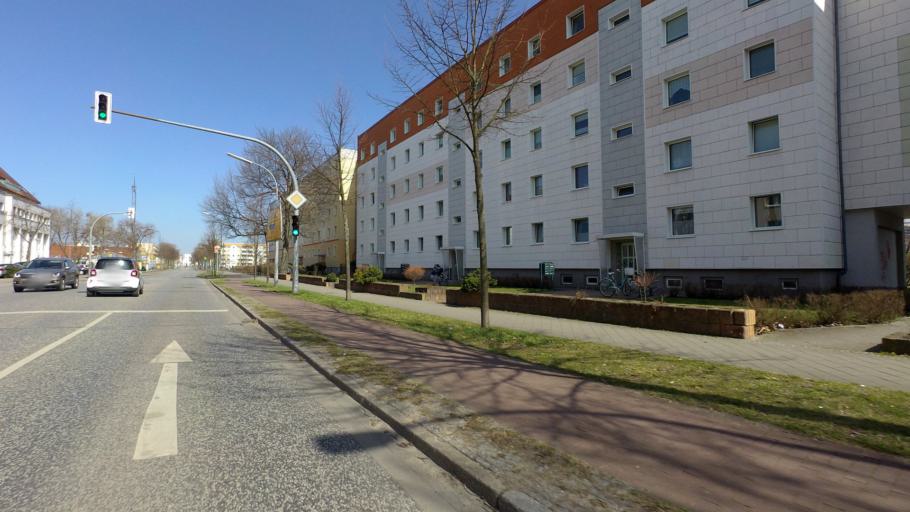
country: DE
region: Brandenburg
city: Oranienburg
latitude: 52.7462
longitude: 13.2375
